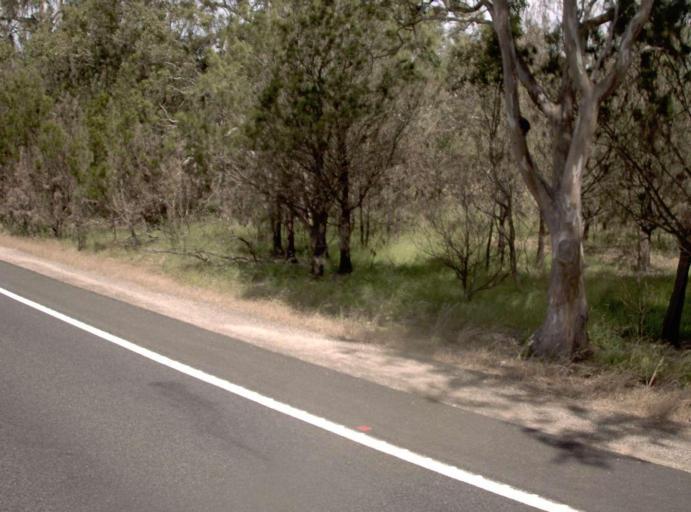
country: AU
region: Victoria
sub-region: East Gippsland
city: Bairnsdale
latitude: -37.8635
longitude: 147.5020
